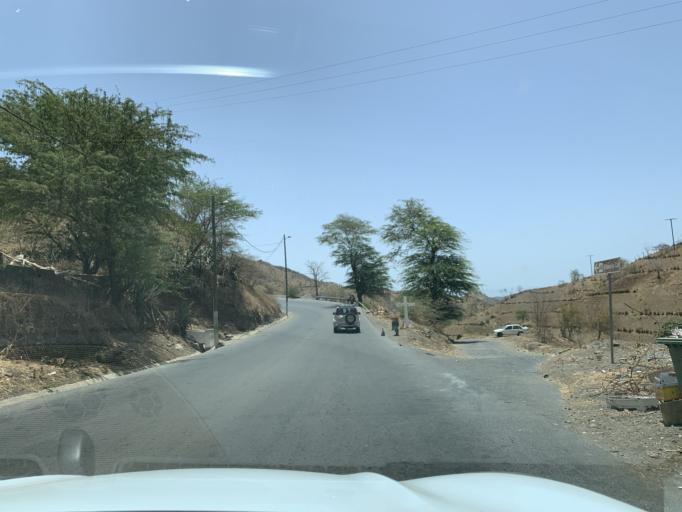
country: CV
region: Sao Domingos
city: Sao Domingos
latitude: 15.0419
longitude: -23.5764
